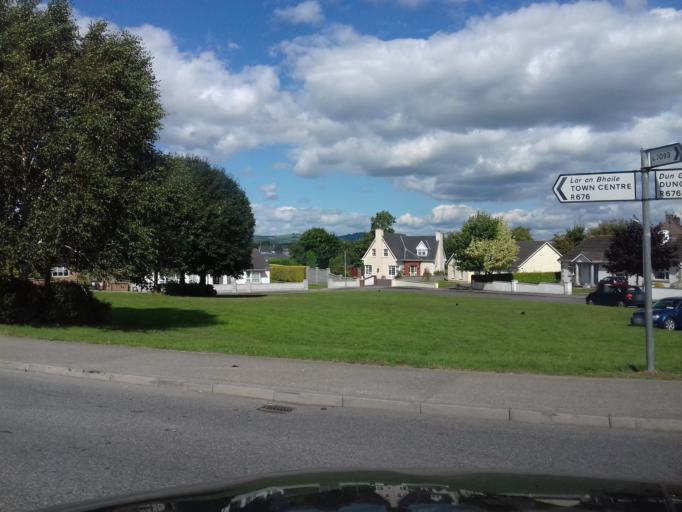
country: IE
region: Munster
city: Carrick-on-Suir
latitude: 52.3421
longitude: -7.4160
